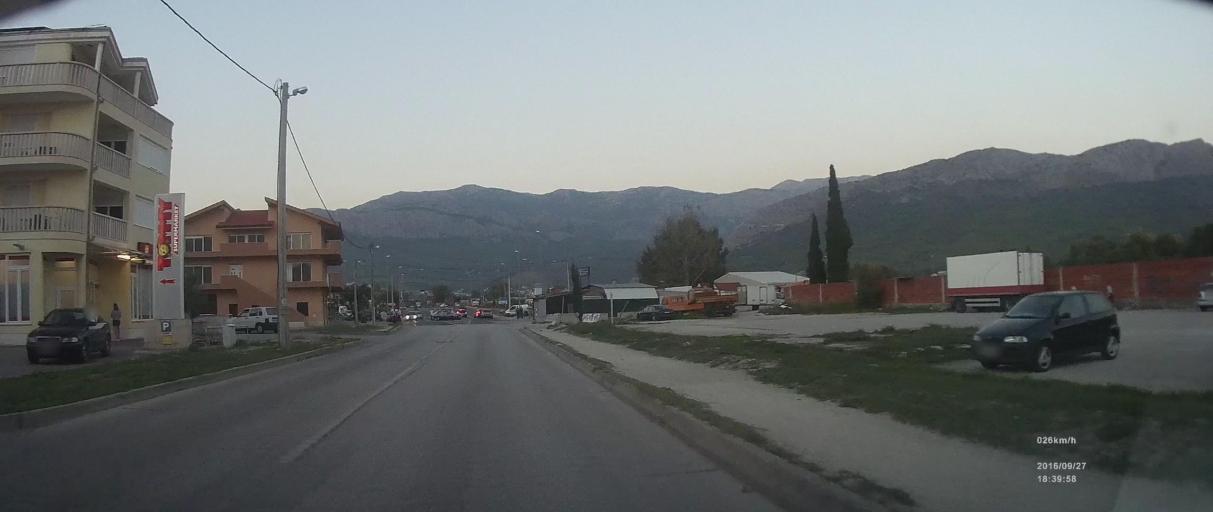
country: HR
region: Splitsko-Dalmatinska
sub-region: Grad Split
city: Stobrec
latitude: 43.5049
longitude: 16.5261
